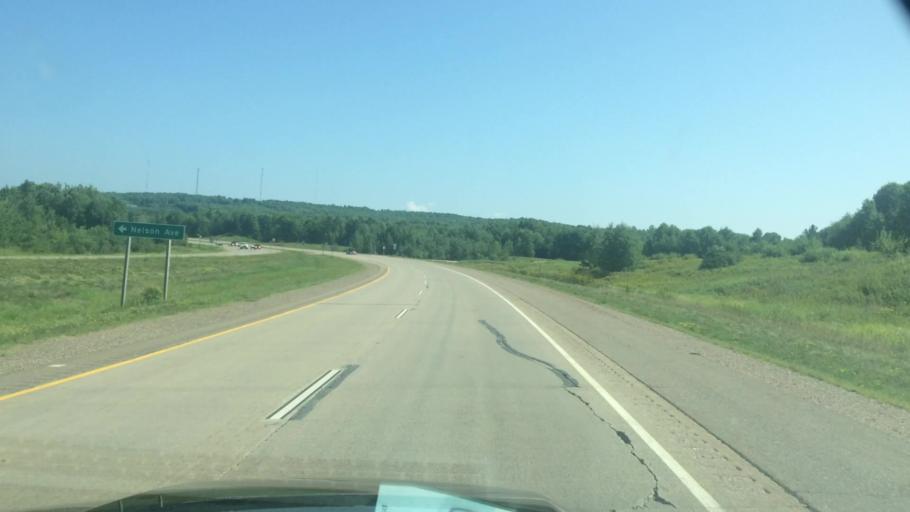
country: US
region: Wisconsin
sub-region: Lincoln County
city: Tomahawk
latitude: 45.3350
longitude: -89.6674
